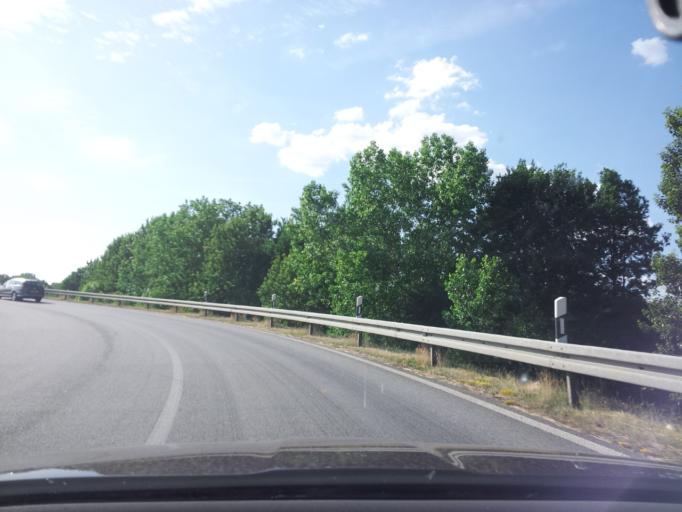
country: DE
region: Brandenburg
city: Trebbin
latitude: 52.2324
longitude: 13.2334
